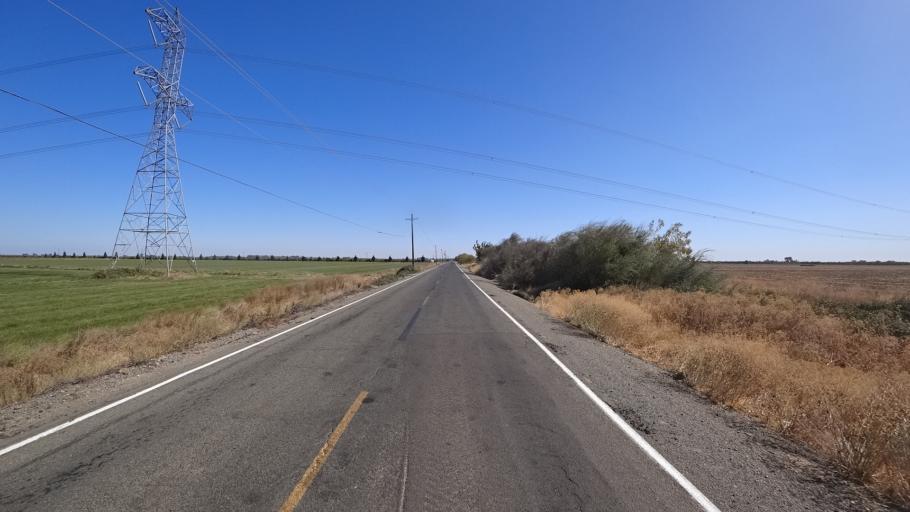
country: US
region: California
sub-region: Yolo County
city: Winters
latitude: 38.5619
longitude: -121.9096
